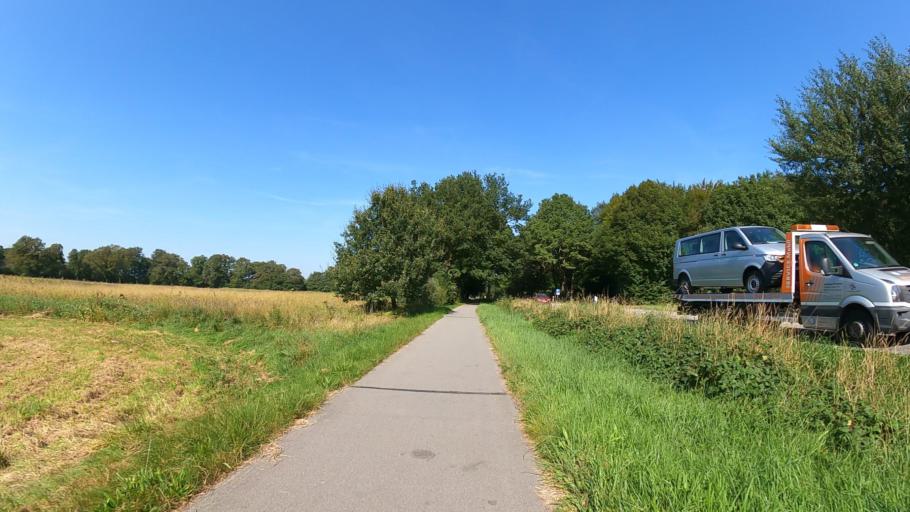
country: DE
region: Schleswig-Holstein
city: Bad Bramstedt
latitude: 53.8953
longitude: 9.8843
